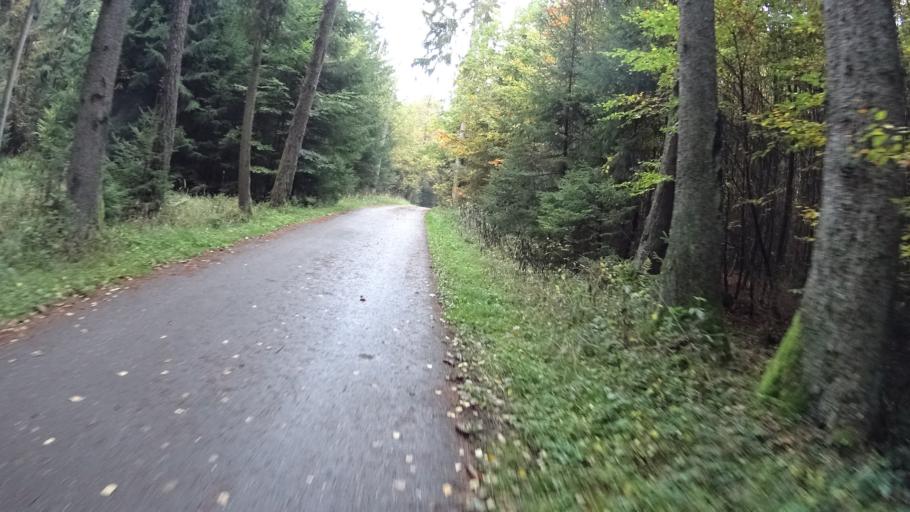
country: DE
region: Bavaria
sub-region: Upper Bavaria
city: Adelschlag
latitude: 48.8424
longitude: 11.2613
